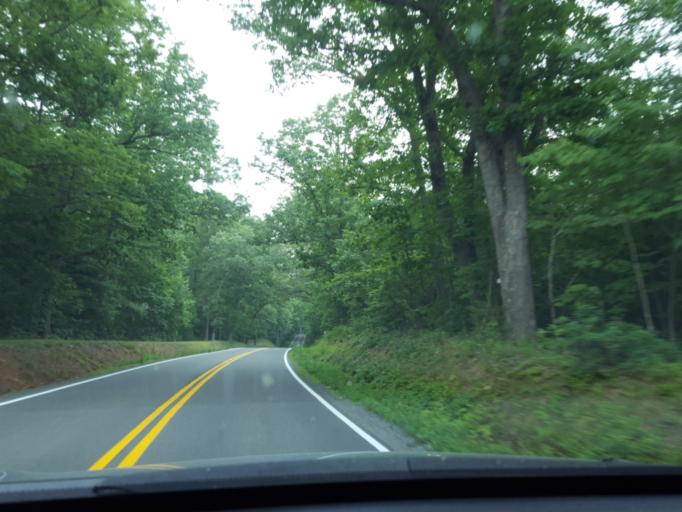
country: US
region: Virginia
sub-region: Spotsylvania County
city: Spotsylvania
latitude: 38.2703
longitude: -77.7968
